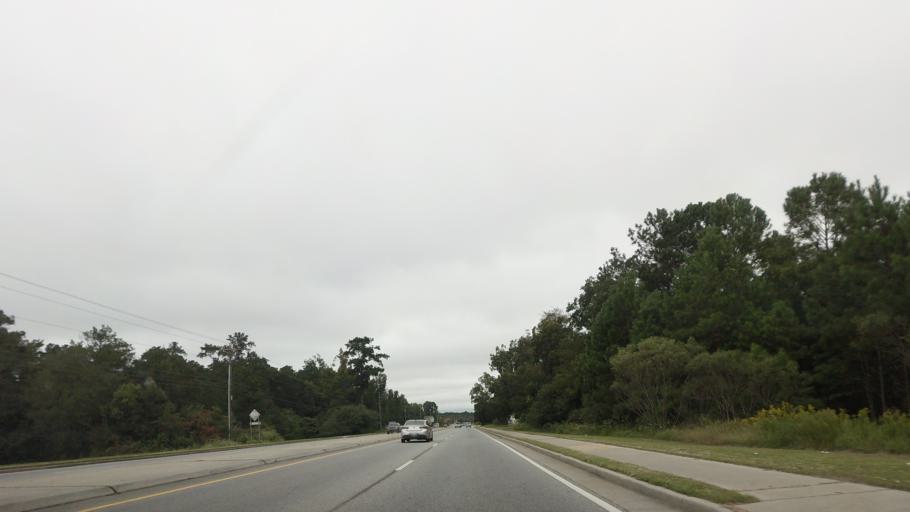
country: US
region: Georgia
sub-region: Lowndes County
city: Valdosta
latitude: 30.9031
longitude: -83.2657
